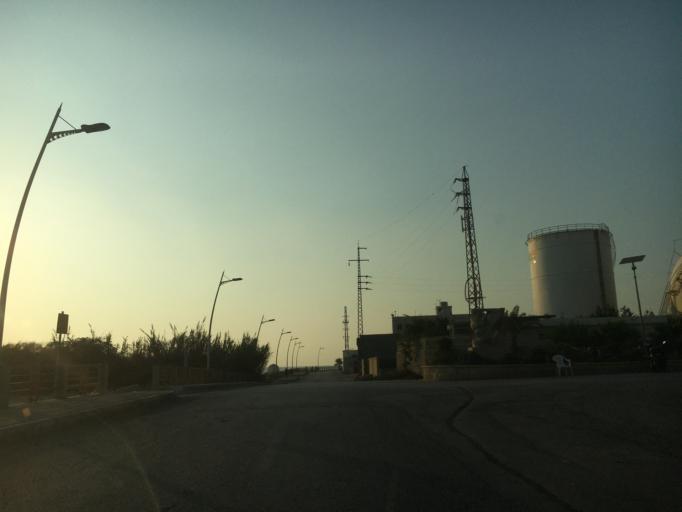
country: LB
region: Mont-Liban
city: Jbail
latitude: 34.1413
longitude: 35.6300
